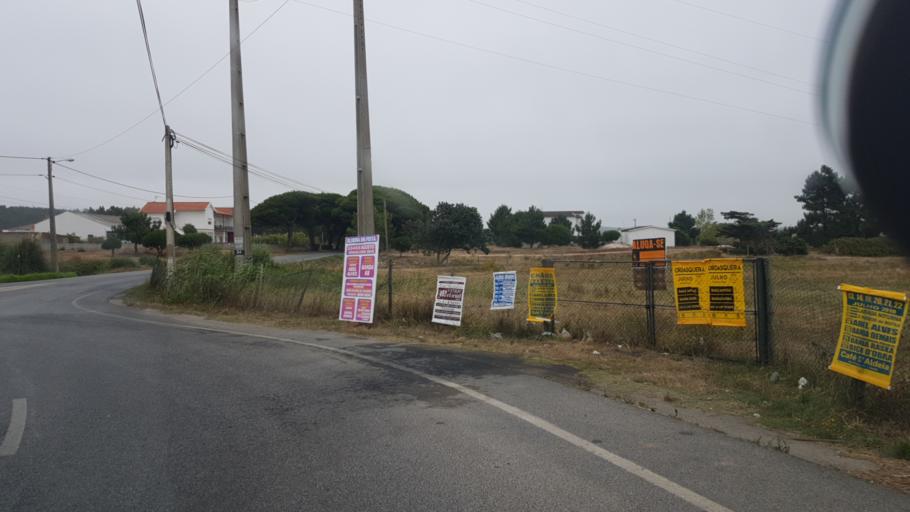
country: PT
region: Lisbon
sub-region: Torres Vedras
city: Silveira
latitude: 39.0927
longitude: -9.3445
